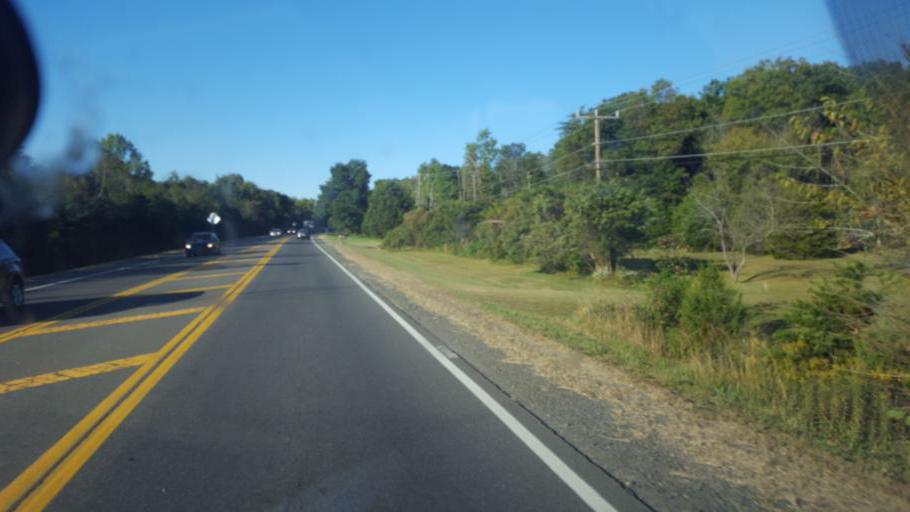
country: US
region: Virginia
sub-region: Prince William County
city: Nokesville
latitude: 38.6977
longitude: -77.5879
